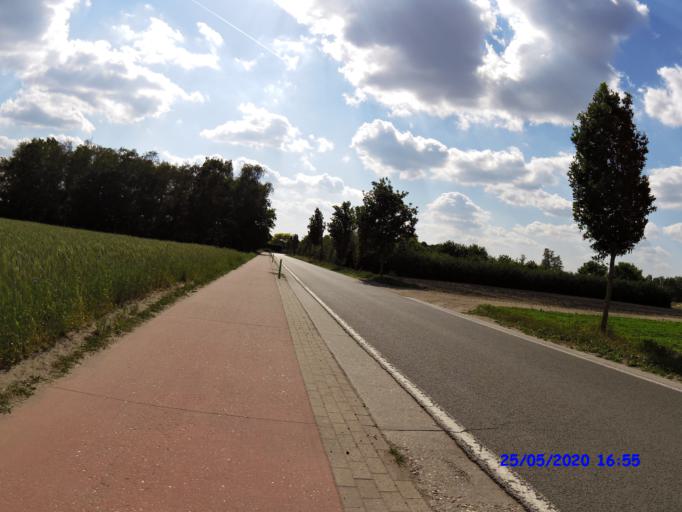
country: BE
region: Flanders
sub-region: Provincie Antwerpen
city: Mol
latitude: 51.1864
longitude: 5.0663
